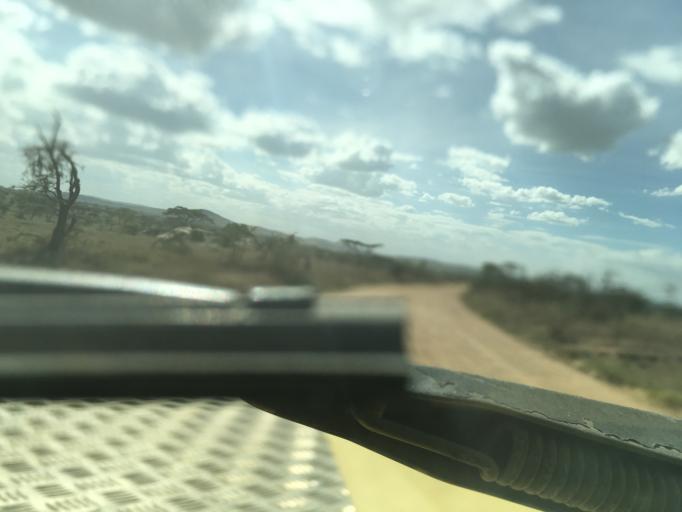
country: TZ
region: Mara
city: Mugumu
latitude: -2.4302
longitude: 34.8284
